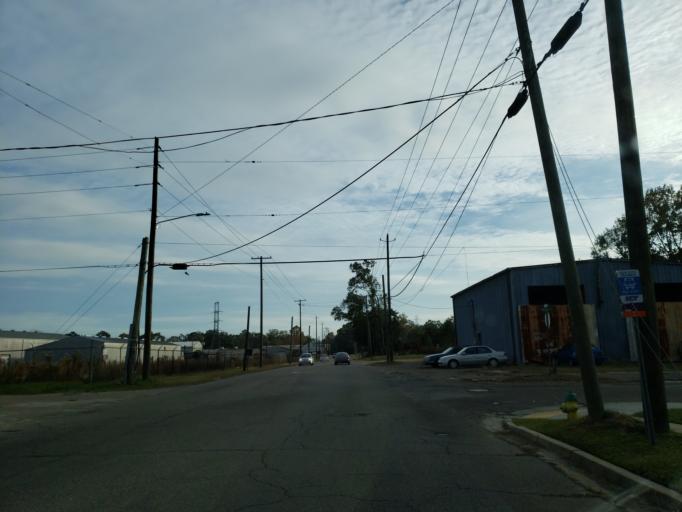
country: US
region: Mississippi
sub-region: Forrest County
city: Hattiesburg
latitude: 31.3064
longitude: -89.2851
